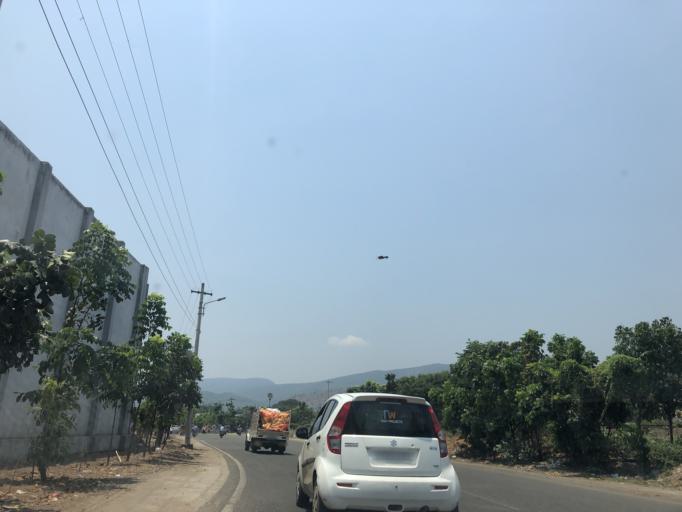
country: IN
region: Andhra Pradesh
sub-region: Vishakhapatnam
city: Yarada
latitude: 17.7158
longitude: 83.2918
